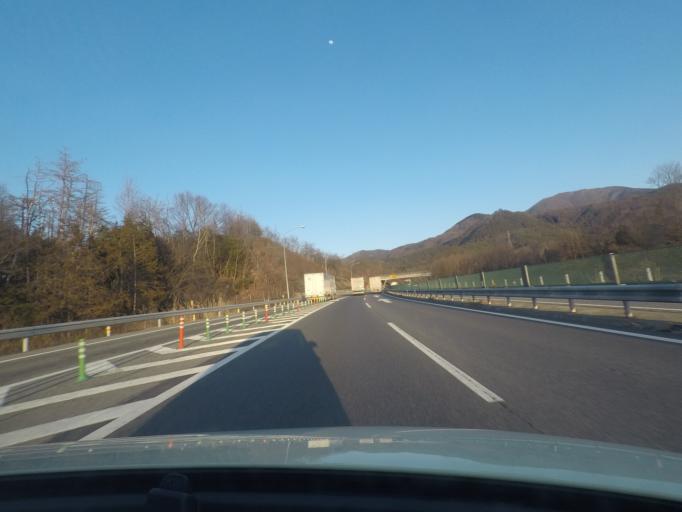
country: JP
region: Nagano
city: Omachi
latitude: 36.4367
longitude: 138.0181
